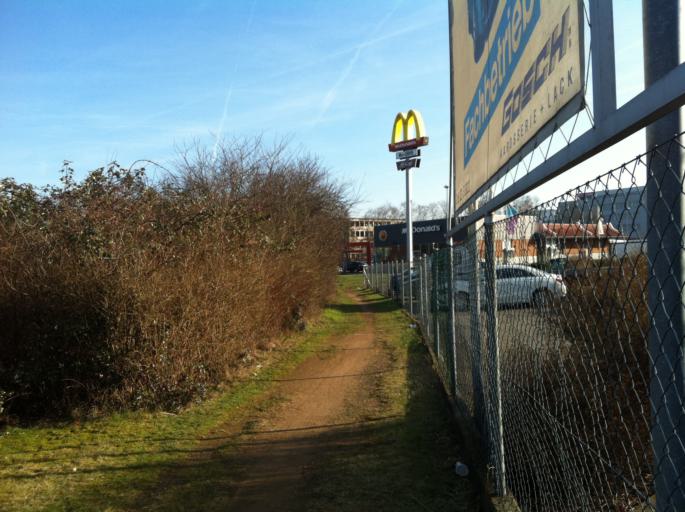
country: DE
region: Hesse
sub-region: Regierungsbezirk Darmstadt
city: Neu Isenburg
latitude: 50.0488
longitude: 8.7166
